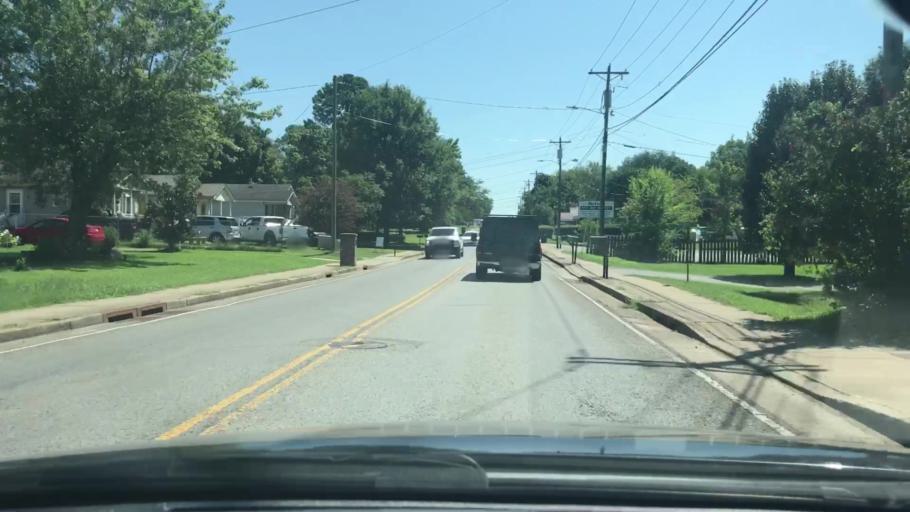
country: US
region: Tennessee
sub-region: Sumner County
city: Gallatin
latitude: 36.3933
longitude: -86.4618
